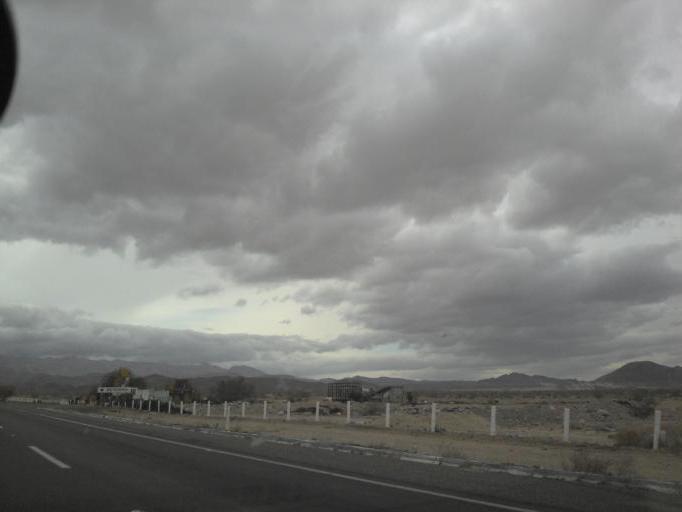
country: US
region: California
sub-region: Imperial County
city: Seeley
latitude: 32.5651
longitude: -115.8873
